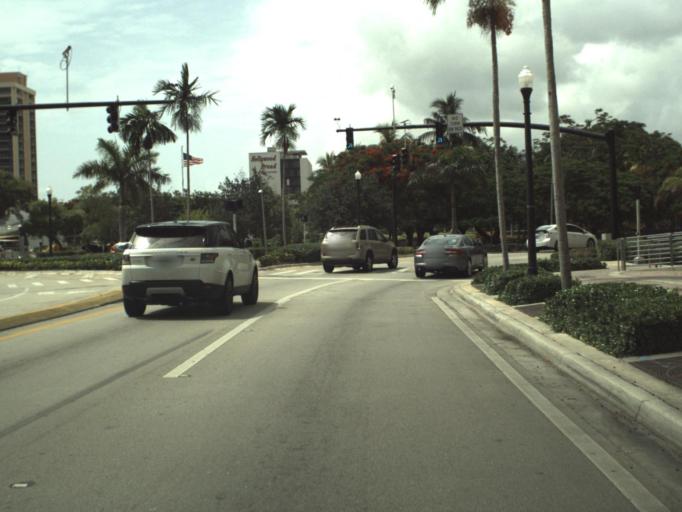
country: US
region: Florida
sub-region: Broward County
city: Hollywood
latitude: 26.0131
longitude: -80.1432
